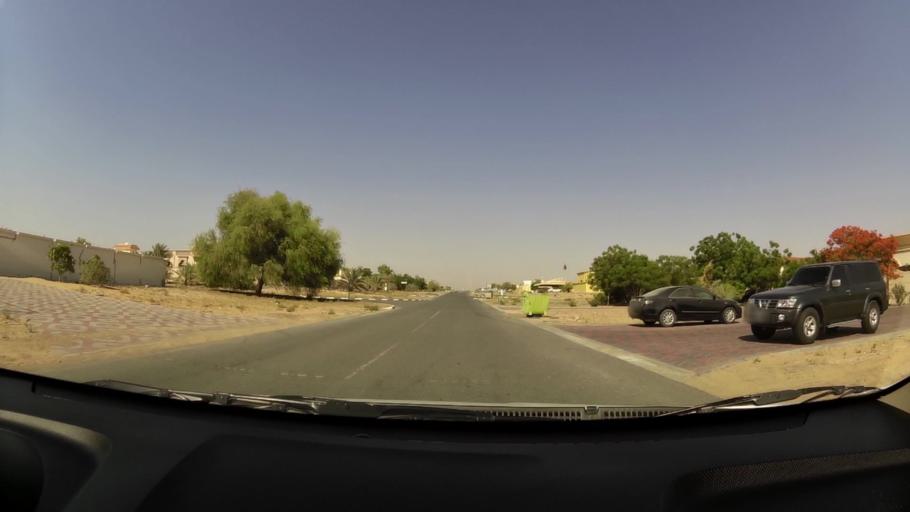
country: AE
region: Umm al Qaywayn
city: Umm al Qaywayn
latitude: 25.4909
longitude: 55.5788
